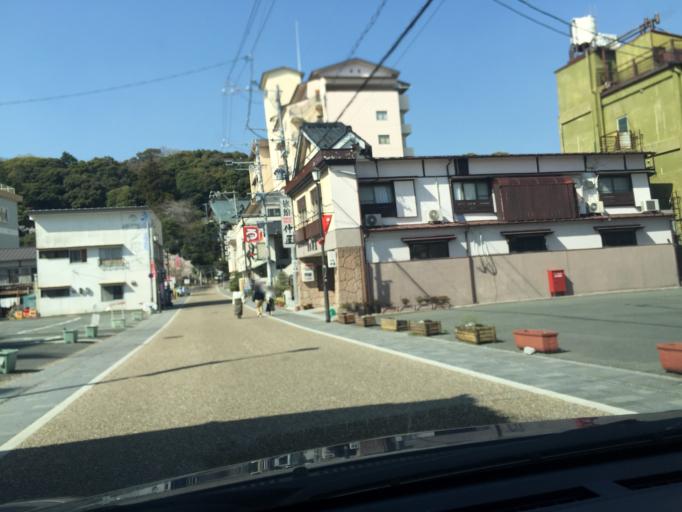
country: JP
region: Shizuoka
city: Kosai-shi
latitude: 34.7667
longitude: 137.6132
